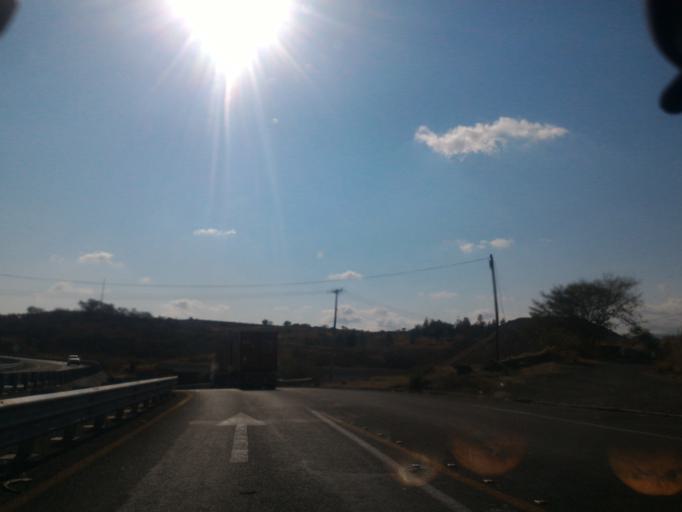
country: MX
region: Jalisco
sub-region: Tonila
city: San Marcos
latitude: 19.4335
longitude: -103.4953
